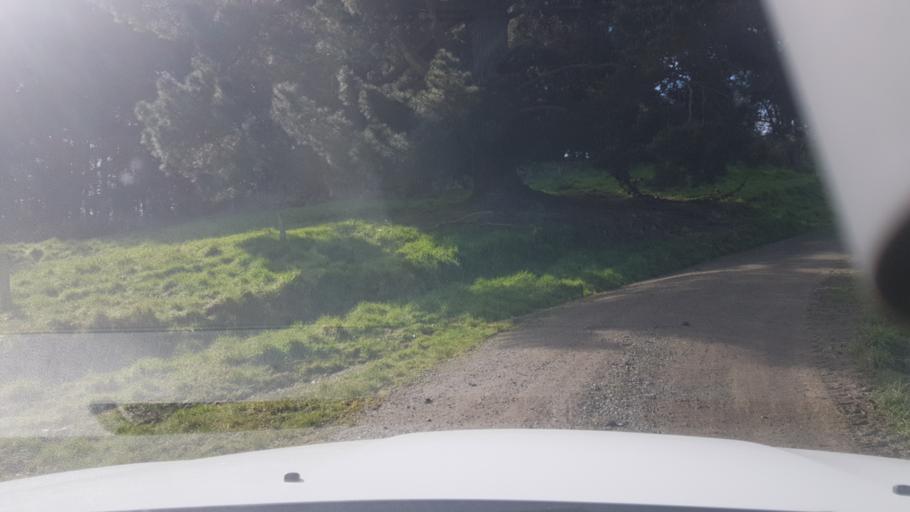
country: NZ
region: Canterbury
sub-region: Timaru District
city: Pleasant Point
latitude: -44.1961
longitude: 171.1879
